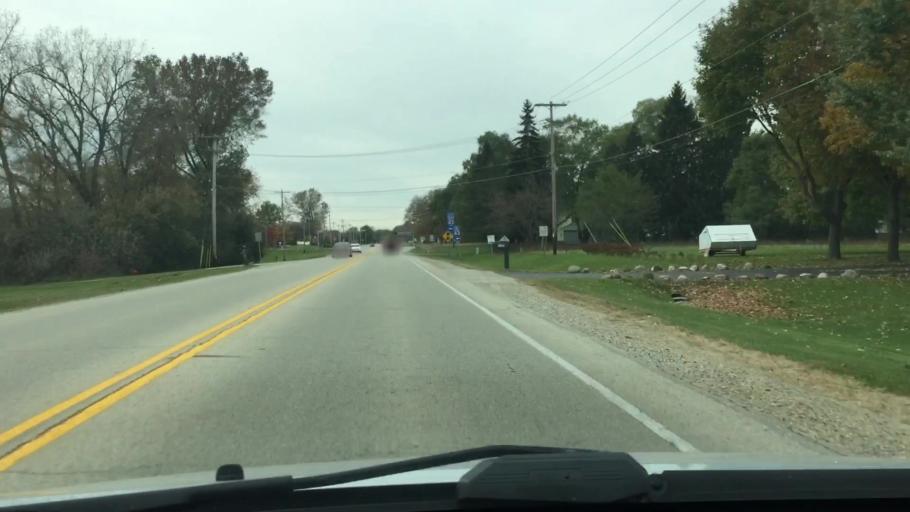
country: US
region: Wisconsin
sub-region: Waukesha County
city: Mukwonago
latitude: 42.8732
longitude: -88.3132
